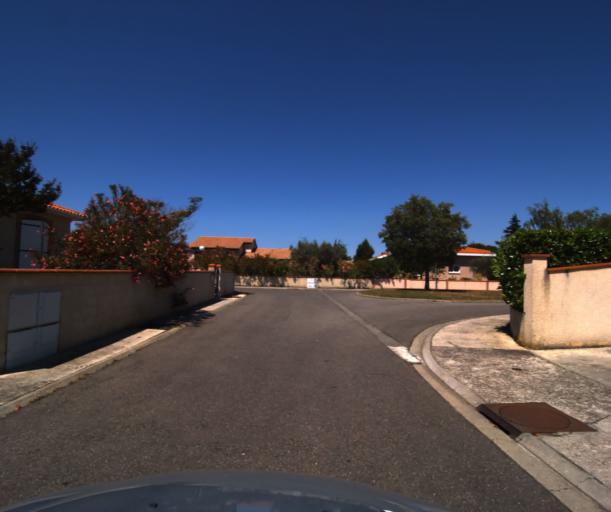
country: FR
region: Midi-Pyrenees
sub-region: Departement de la Haute-Garonne
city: Muret
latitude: 43.4517
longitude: 1.3266
